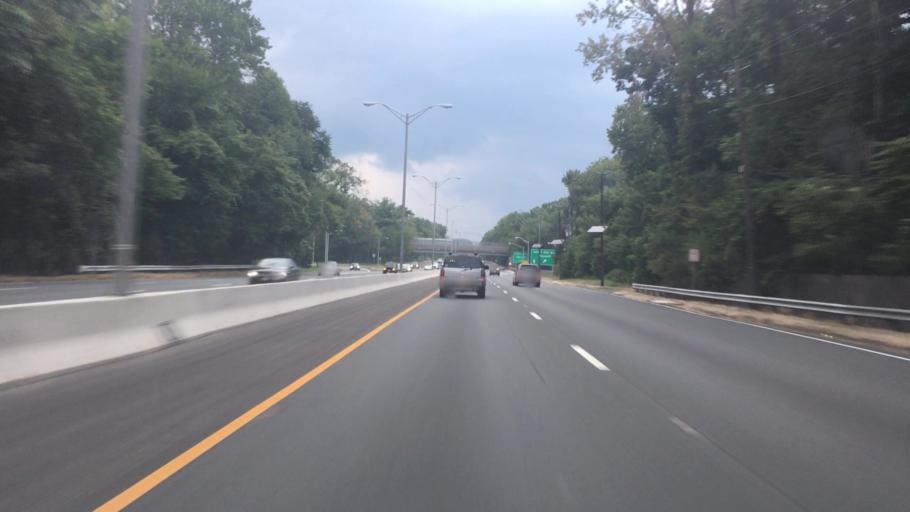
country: US
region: New Jersey
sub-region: Bergen County
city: Midland Park
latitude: 40.9852
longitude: -74.1654
